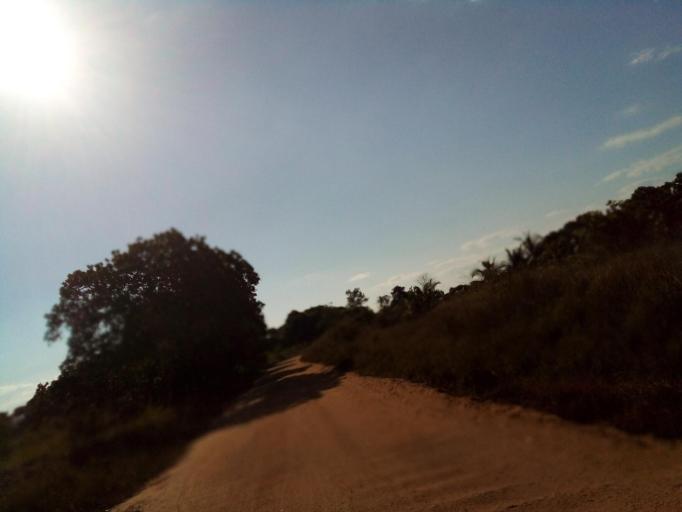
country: MZ
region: Zambezia
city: Quelimane
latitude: -17.5329
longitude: 36.6207
